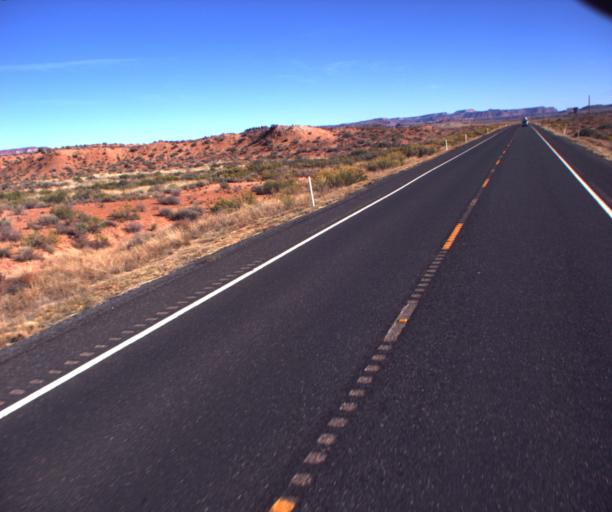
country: US
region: Arizona
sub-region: Coconino County
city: Fredonia
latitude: 36.9161
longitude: -112.5796
